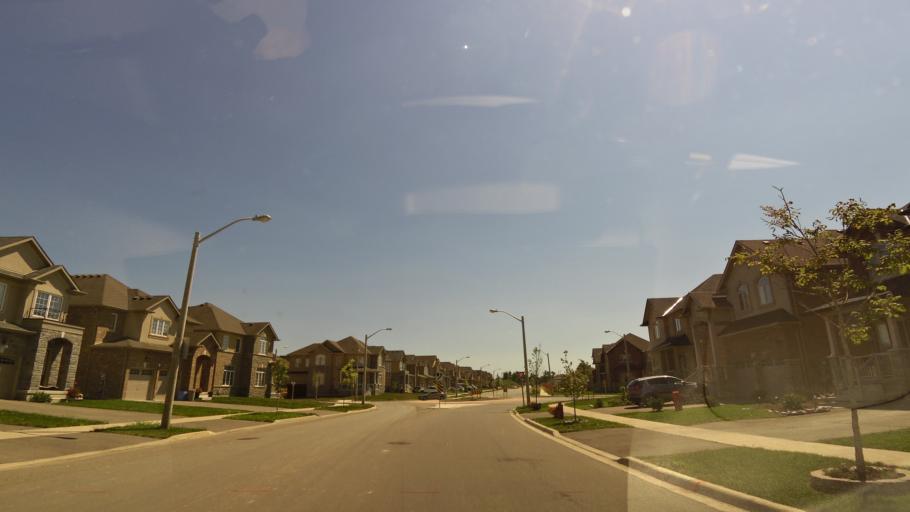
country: CA
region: Ontario
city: Ancaster
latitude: 43.2148
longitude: -79.9361
